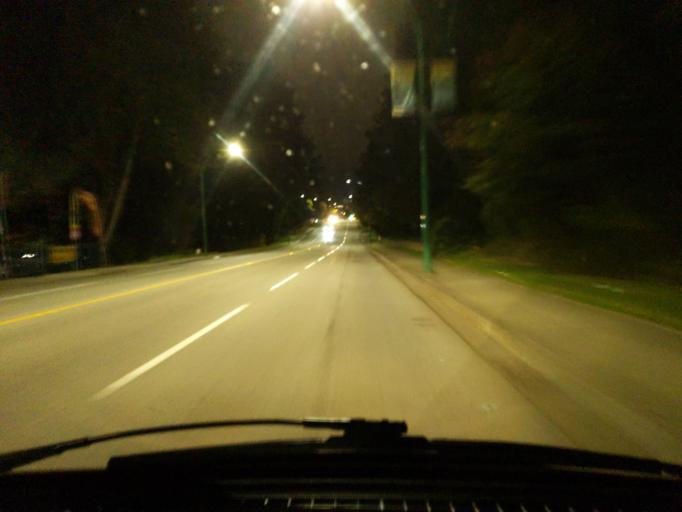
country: CA
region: British Columbia
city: Burnaby
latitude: 49.2546
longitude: -123.0184
